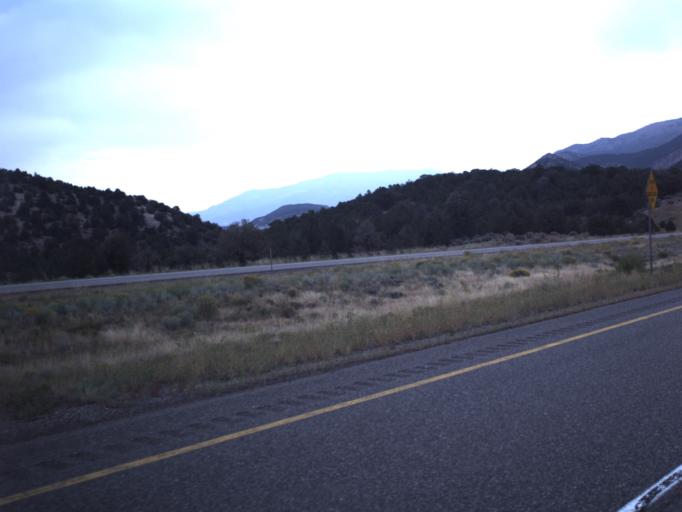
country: US
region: Utah
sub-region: Sevier County
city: Monroe
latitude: 38.5498
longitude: -112.3868
